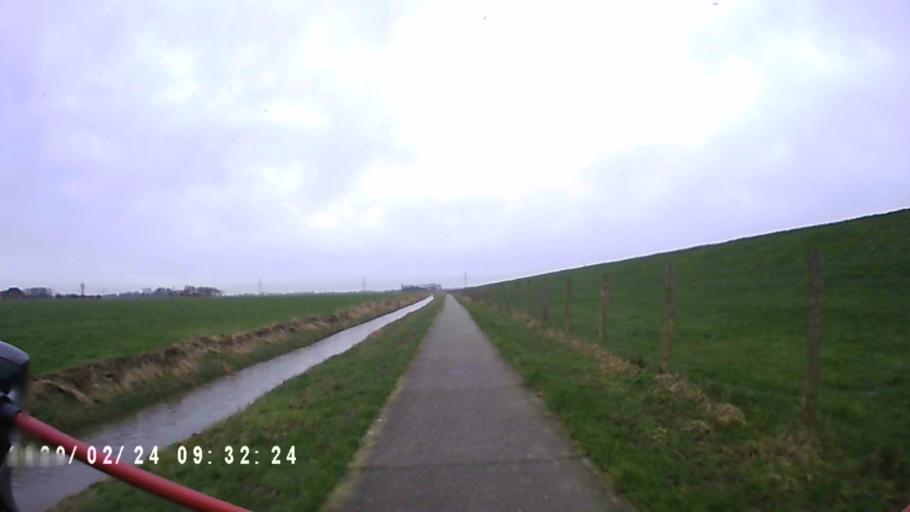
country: NL
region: Groningen
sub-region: Gemeente Winsum
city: Winsum
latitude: 53.3043
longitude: 6.4968
